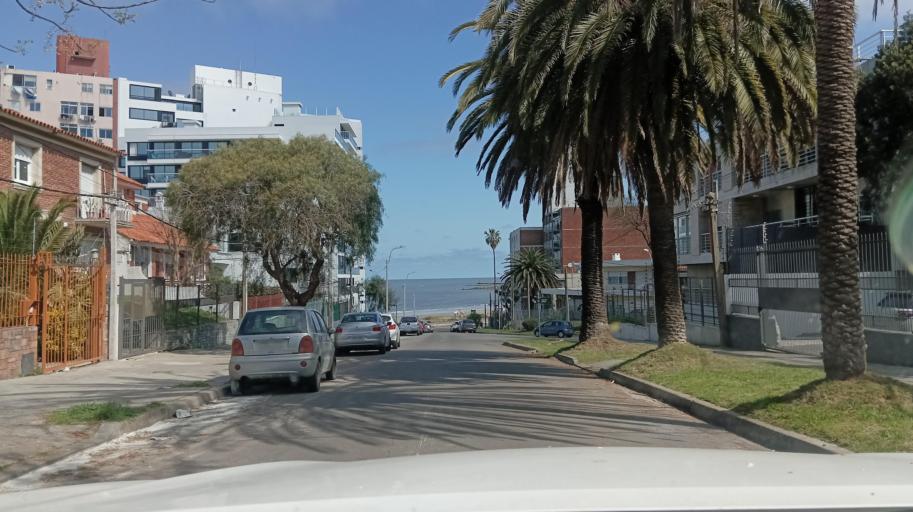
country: UY
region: Montevideo
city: Montevideo
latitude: -34.8957
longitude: -56.1165
